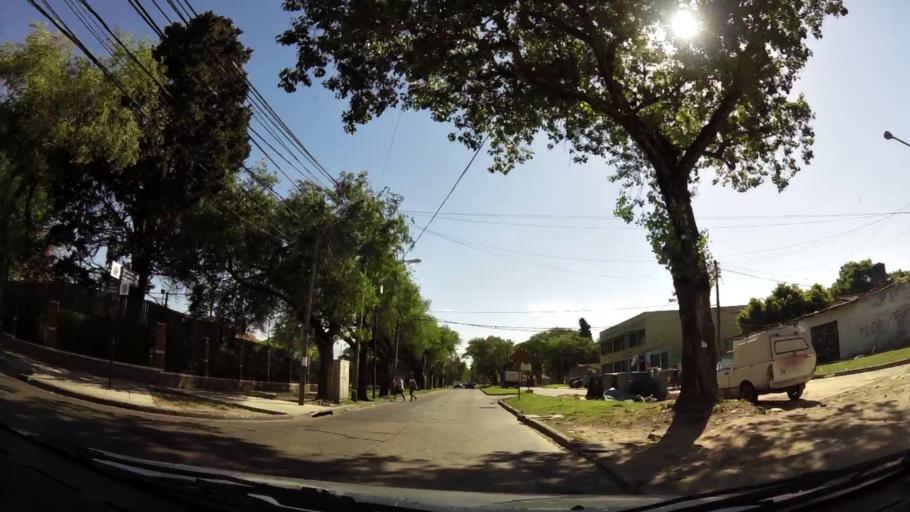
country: AR
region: Buenos Aires
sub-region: Partido de San Isidro
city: San Isidro
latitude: -34.4736
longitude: -58.5398
